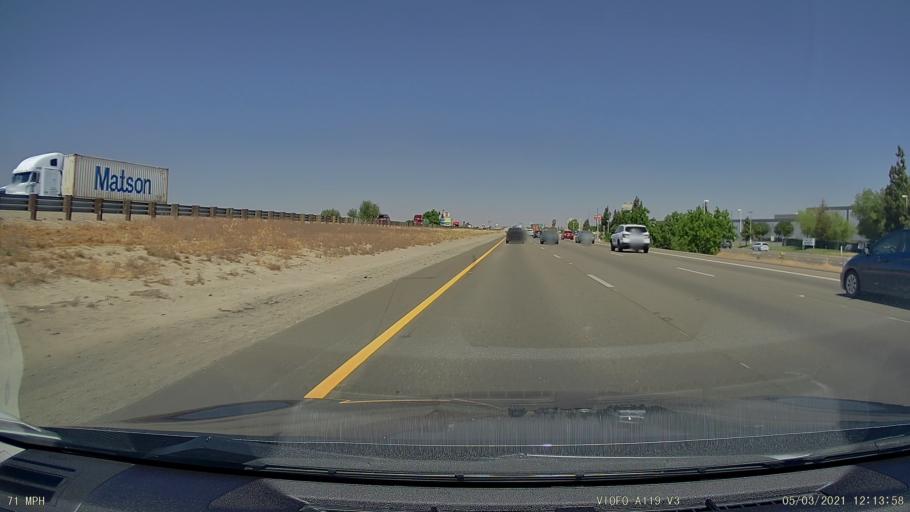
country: US
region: California
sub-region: San Joaquin County
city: Lathrop
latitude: 37.8043
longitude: -121.2973
